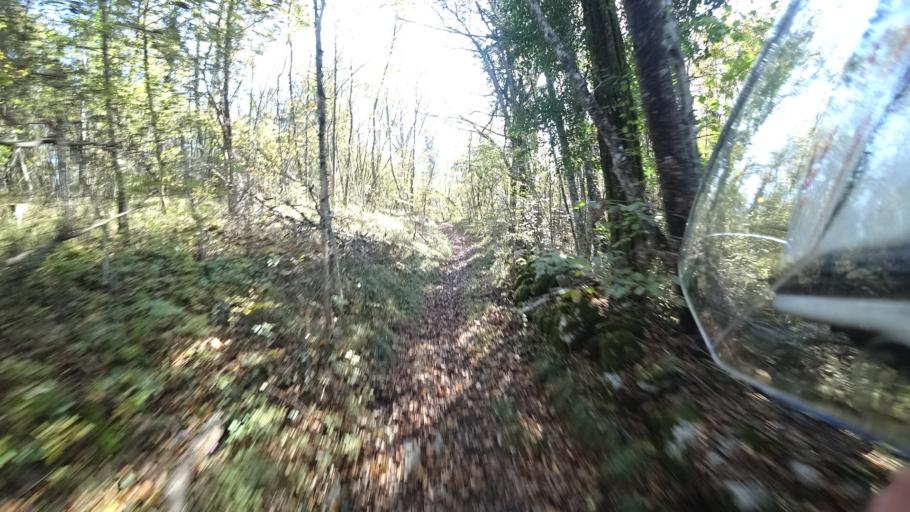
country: HR
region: Primorsko-Goranska
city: Matulji
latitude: 45.3959
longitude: 14.2970
